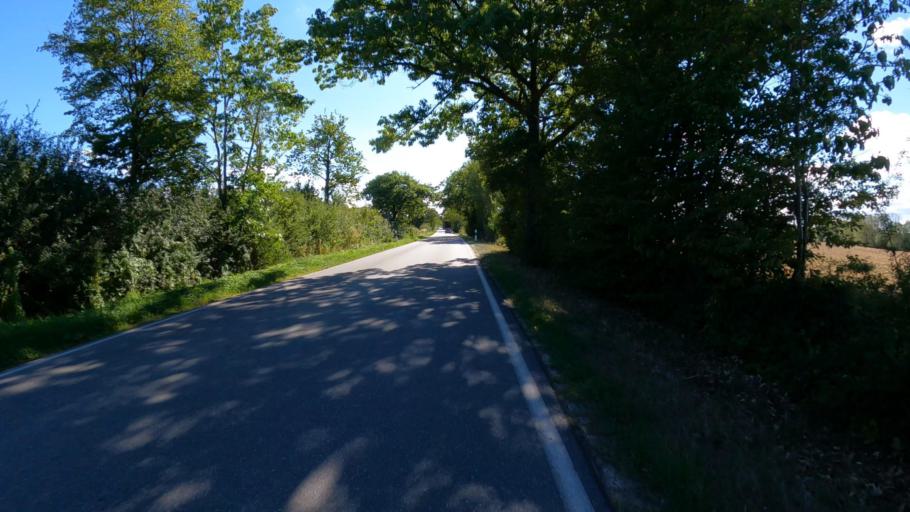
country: DE
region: Schleswig-Holstein
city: Gross Boden
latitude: 53.7464
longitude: 10.4501
